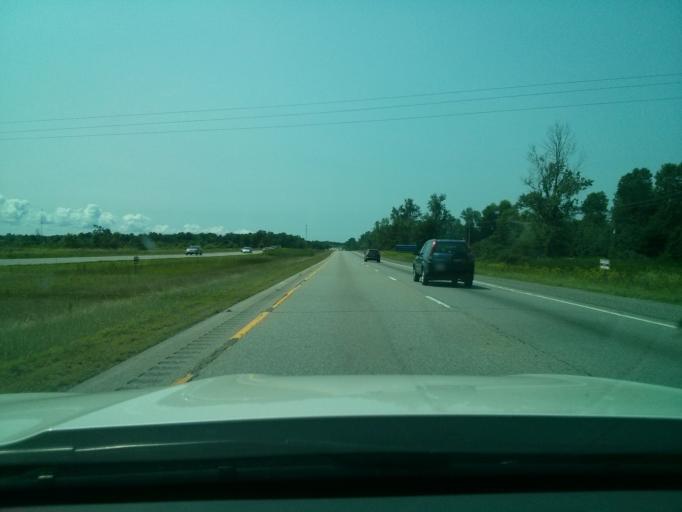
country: CA
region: Ontario
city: Brockville
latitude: 44.6658
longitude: -75.6108
